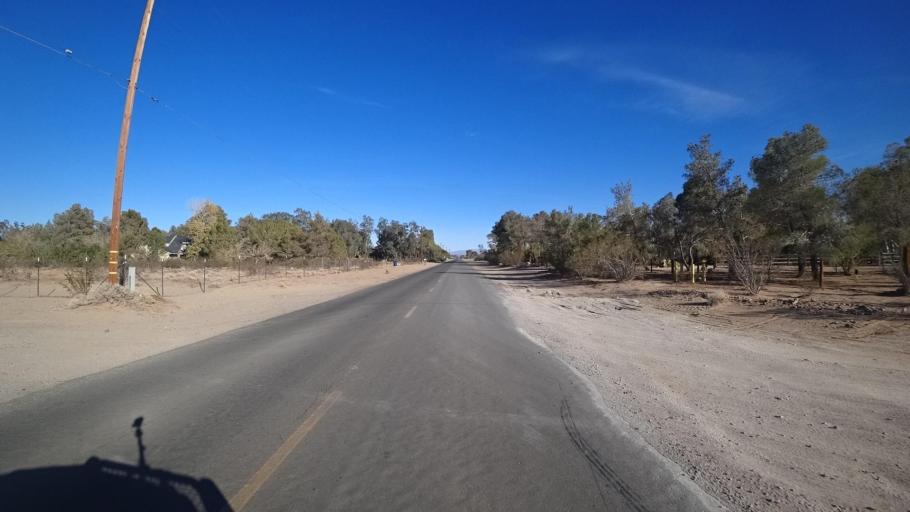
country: US
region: California
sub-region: Kern County
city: Ridgecrest
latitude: 35.6372
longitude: -117.7100
